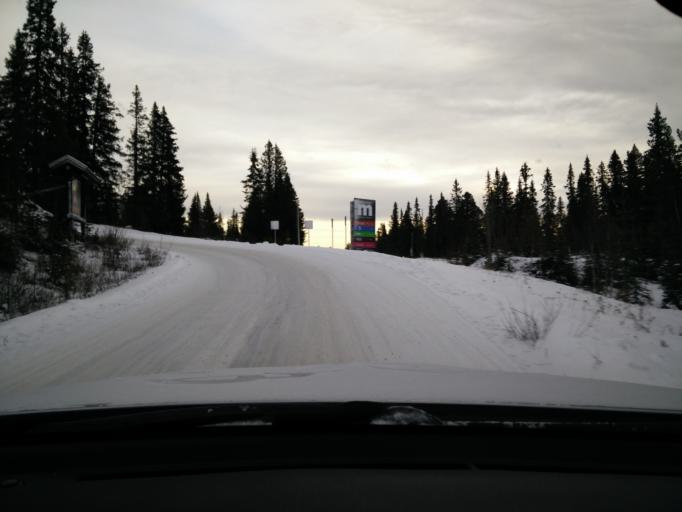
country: SE
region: Jaemtland
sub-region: Bergs Kommun
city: Hoverberg
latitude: 62.4790
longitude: 14.1293
